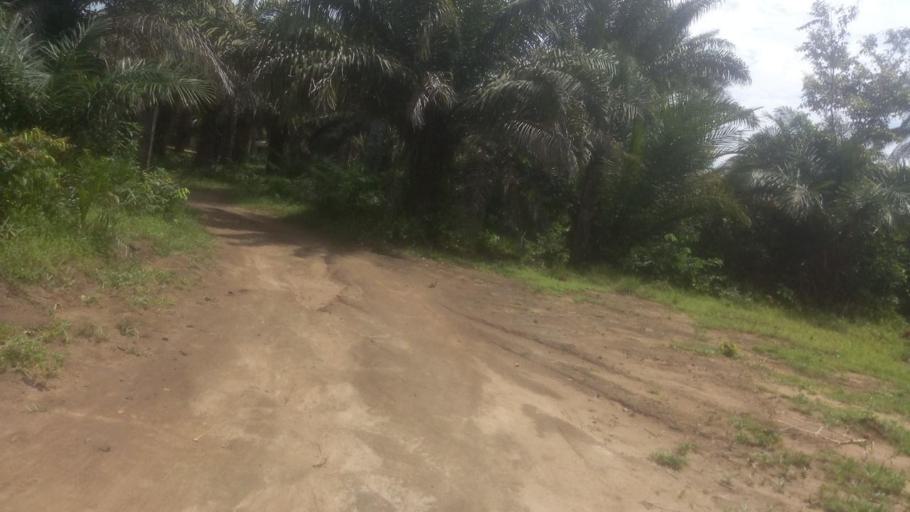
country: SL
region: Northern Province
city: Masoyila
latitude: 8.5455
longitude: -13.1602
